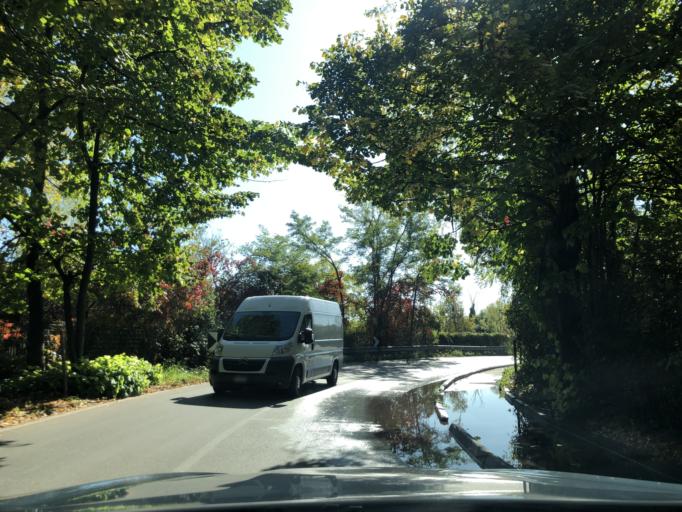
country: IT
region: Lombardy
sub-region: Provincia di Monza e Brianza
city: Villaggio del Sole
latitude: 45.6222
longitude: 9.1195
